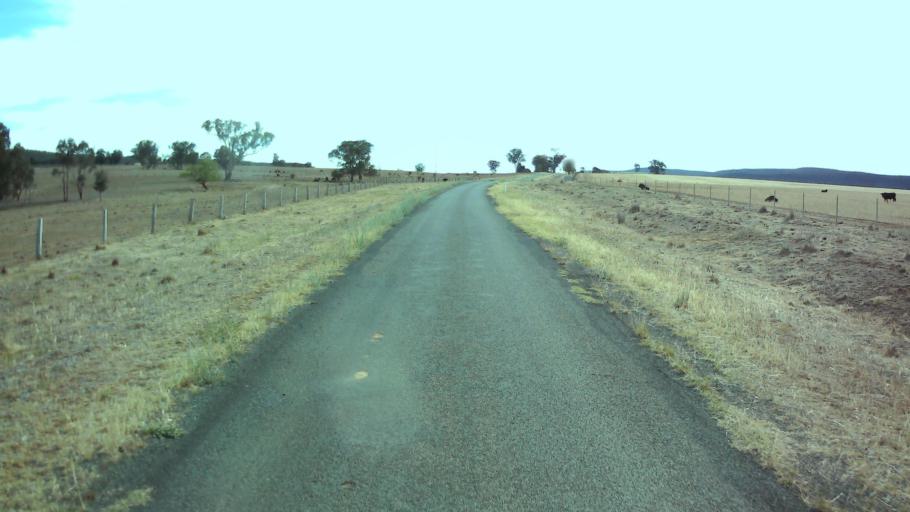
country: AU
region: New South Wales
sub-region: Weddin
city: Grenfell
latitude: -33.8360
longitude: 148.2692
